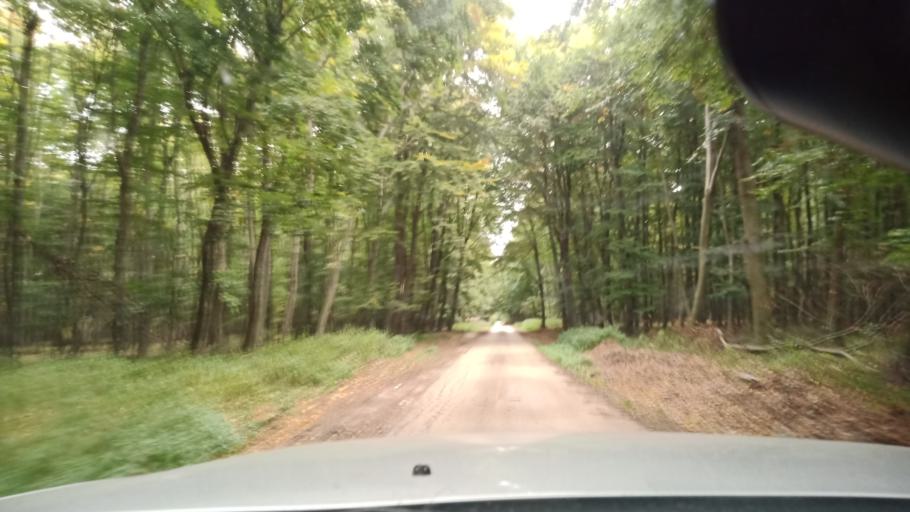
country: HU
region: Fejer
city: Pusztavam
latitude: 47.3948
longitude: 18.2971
